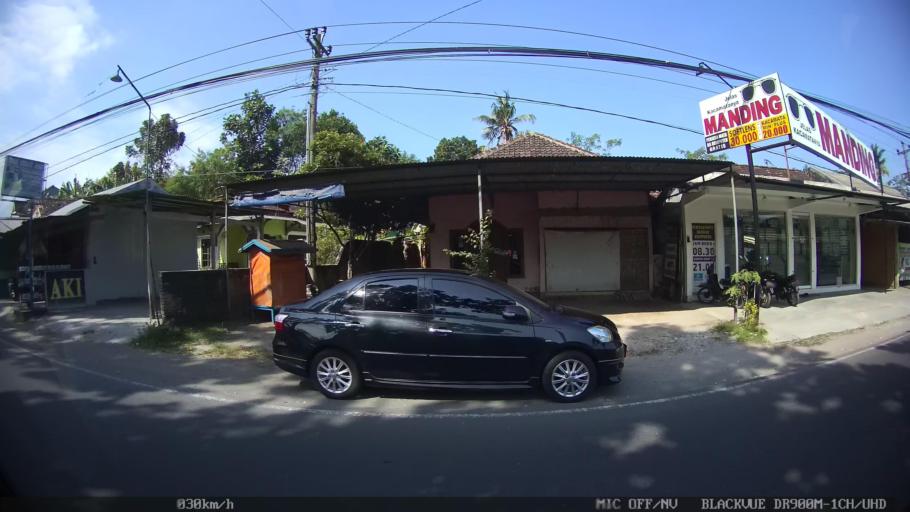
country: ID
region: Daerah Istimewa Yogyakarta
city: Sewon
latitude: -7.8677
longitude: 110.3904
